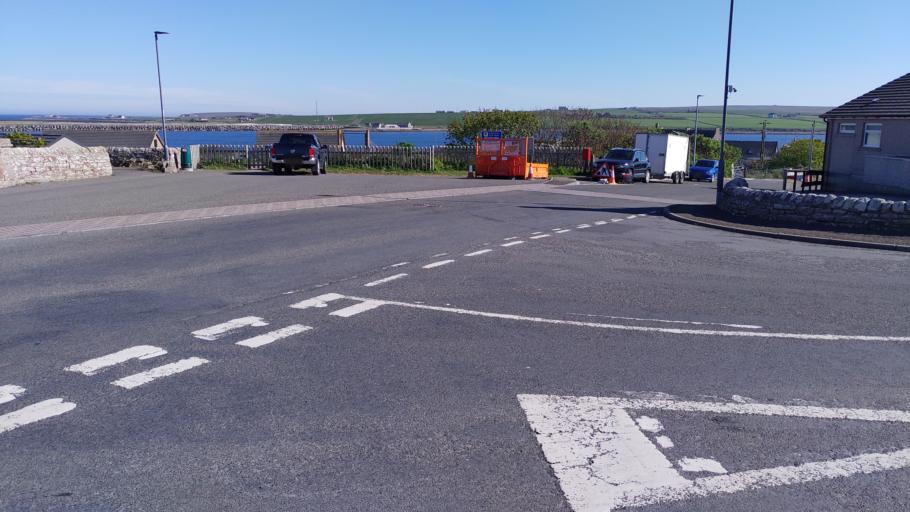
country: GB
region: Scotland
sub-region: Orkney Islands
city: Kirkwall
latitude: 58.8464
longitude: -2.9147
